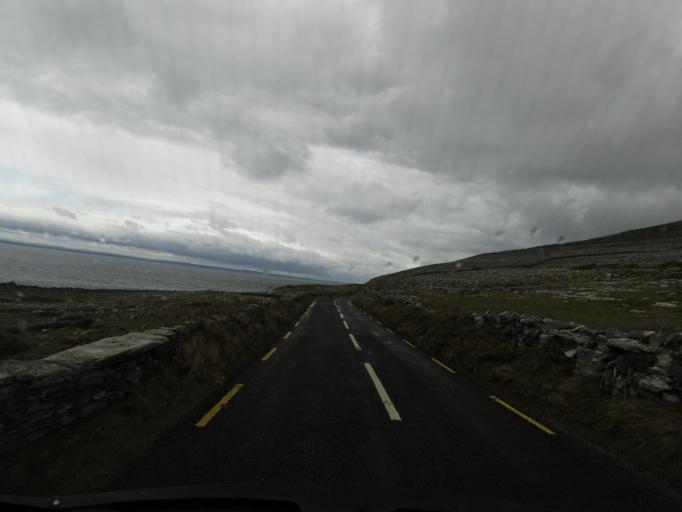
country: IE
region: Connaught
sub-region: County Galway
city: Bearna
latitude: 53.1470
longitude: -9.2716
